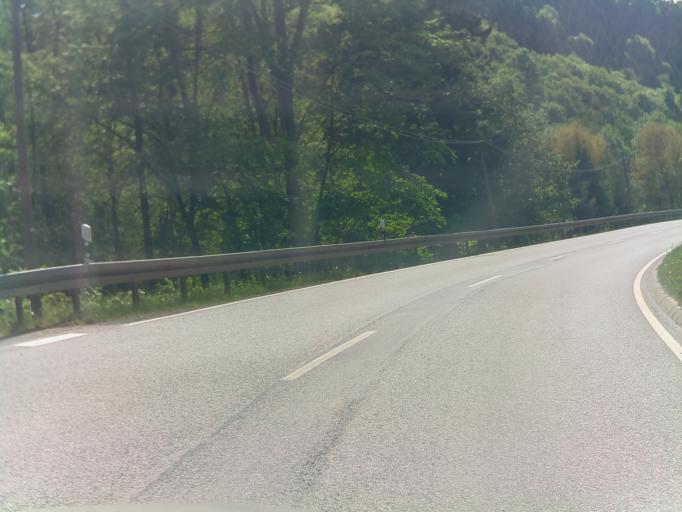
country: DE
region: Thuringia
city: Ilfeld
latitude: 51.6204
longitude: 10.8120
